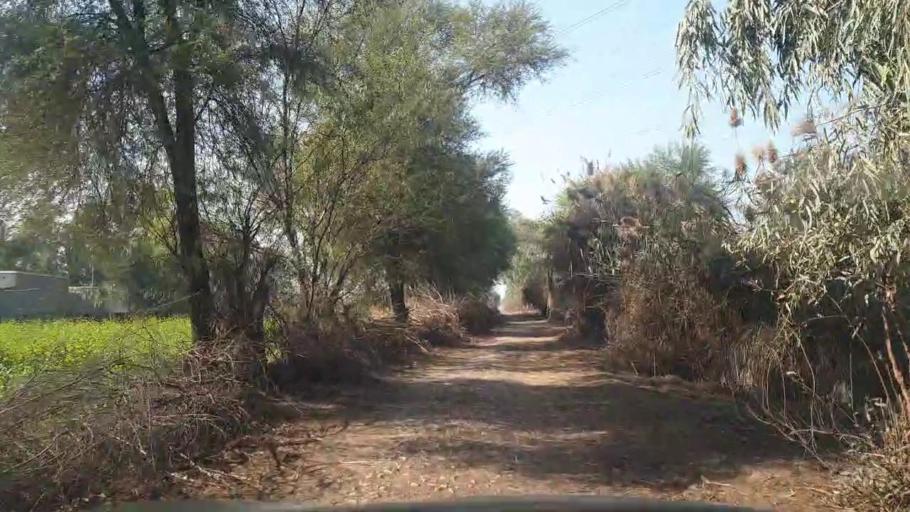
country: PK
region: Sindh
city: Mirpur Mathelo
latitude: 27.9879
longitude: 69.4714
